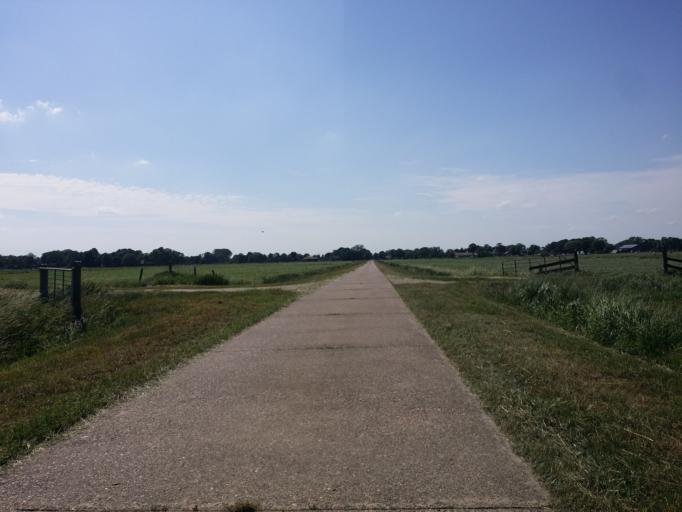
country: DE
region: Lower Saxony
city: Elsfleth
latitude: 53.2021
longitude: 8.3996
